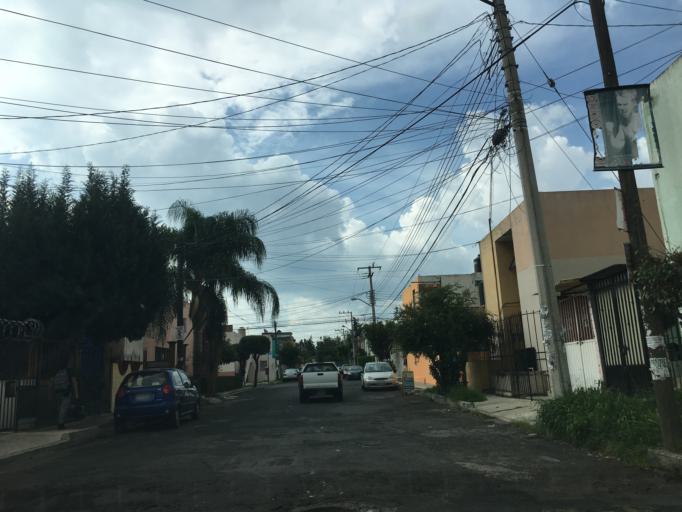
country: MX
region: Michoacan
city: Morelia
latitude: 19.6850
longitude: -101.2045
